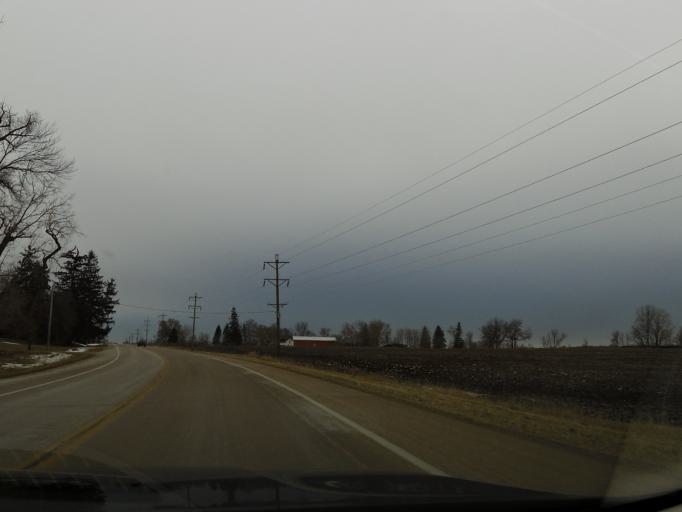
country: US
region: Minnesota
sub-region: Carver County
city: Watertown
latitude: 44.9294
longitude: -93.8325
